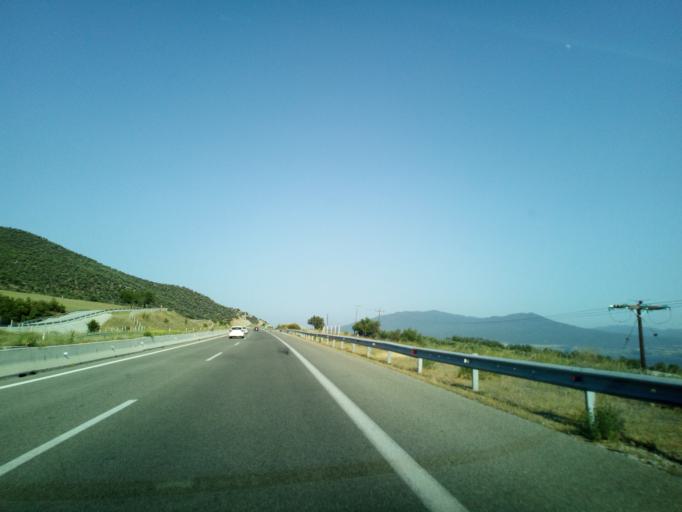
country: GR
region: Central Macedonia
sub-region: Nomos Thessalonikis
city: Nea Apollonia
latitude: 40.6835
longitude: 23.5525
